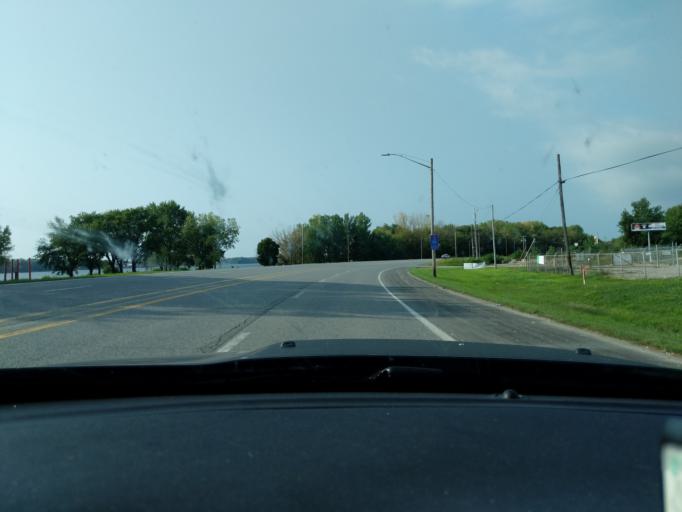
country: US
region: Illinois
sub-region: Rock Island County
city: Rock Island
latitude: 41.5122
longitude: -90.6034
